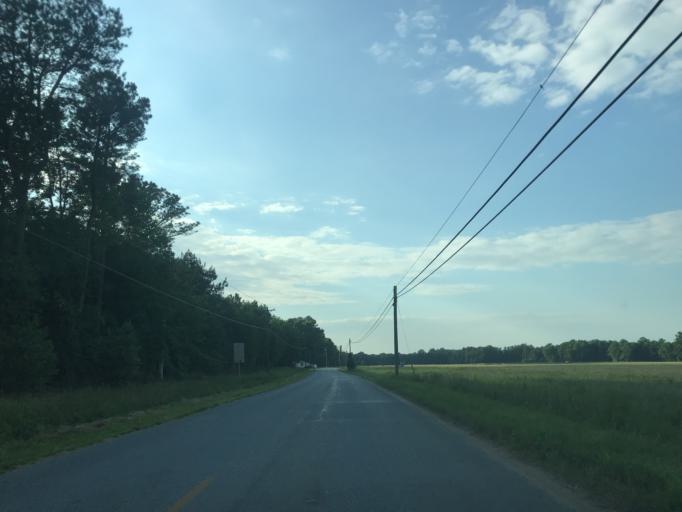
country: US
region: Maryland
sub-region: Caroline County
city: Federalsburg
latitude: 38.7156
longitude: -75.7790
